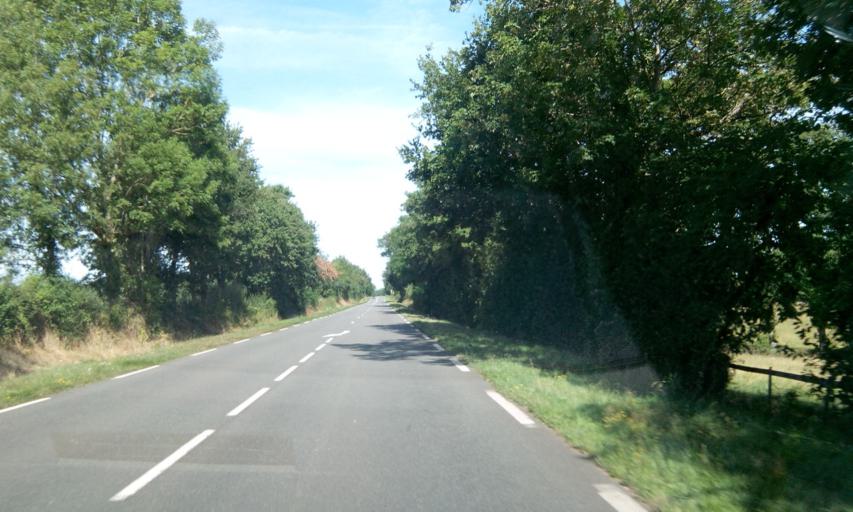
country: FR
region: Poitou-Charentes
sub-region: Departement de la Charente
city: Chabanais
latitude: 45.9475
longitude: 0.7214
